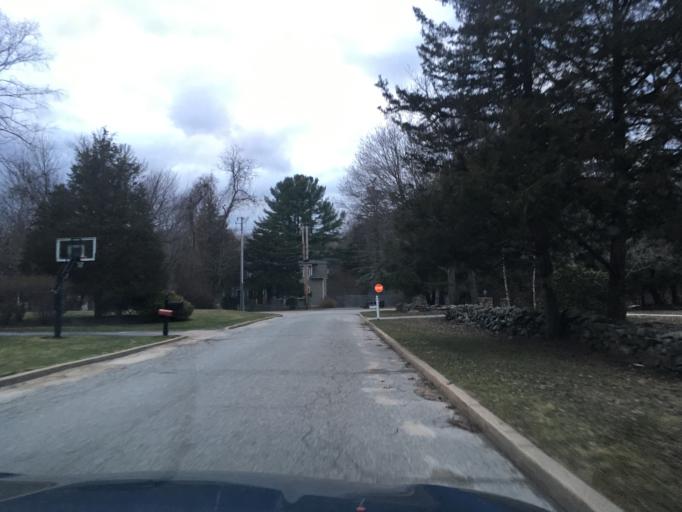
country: US
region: Rhode Island
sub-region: Washington County
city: Exeter
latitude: 41.6219
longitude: -71.5244
